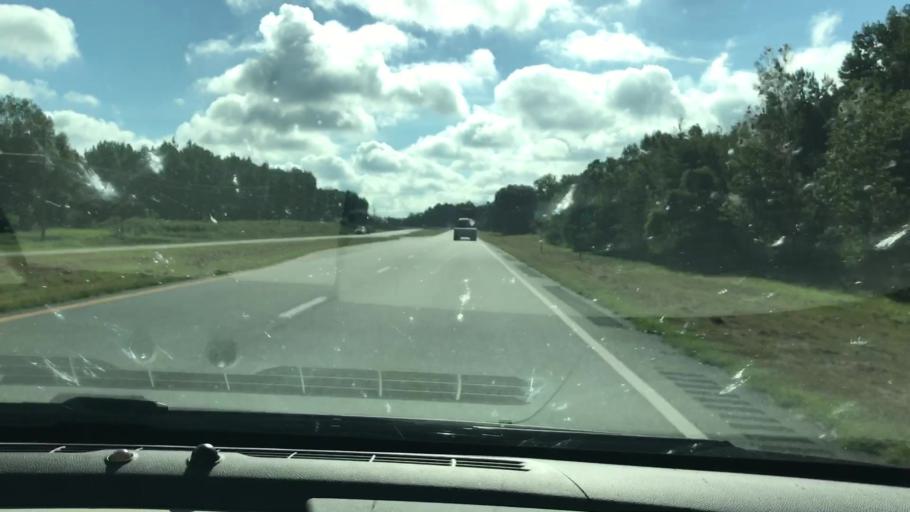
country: US
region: Georgia
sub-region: Worth County
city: Sylvester
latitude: 31.5513
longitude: -83.9729
